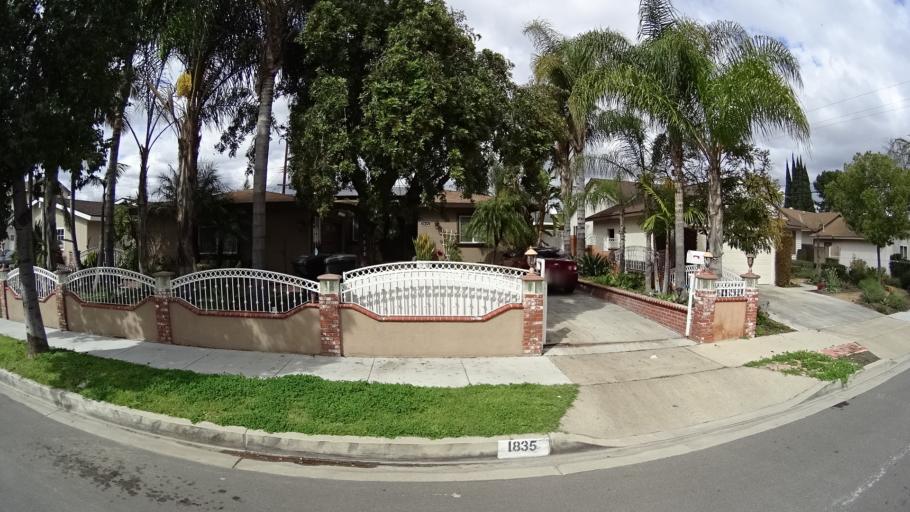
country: US
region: California
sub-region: Orange County
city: Anaheim
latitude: 33.8245
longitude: -117.9477
